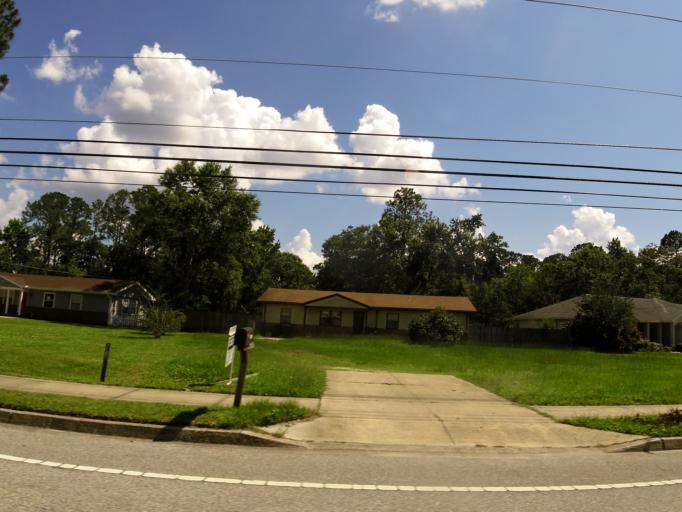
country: US
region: Florida
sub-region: Saint Johns County
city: Fruit Cove
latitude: 30.1479
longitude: -81.5726
